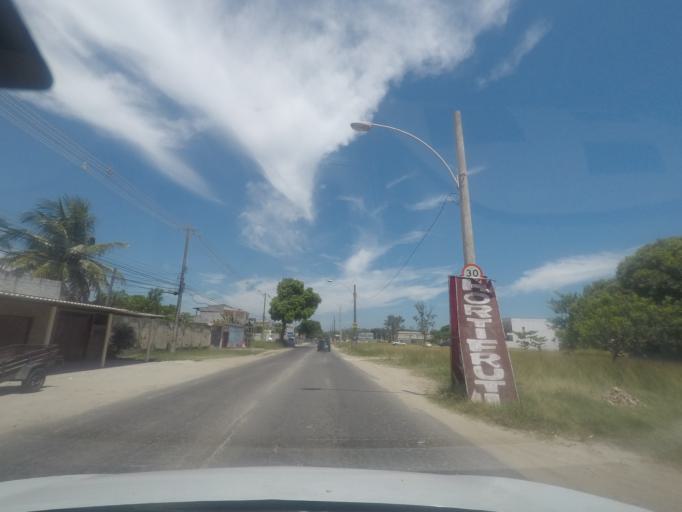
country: BR
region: Rio de Janeiro
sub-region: Itaguai
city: Itaguai
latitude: -22.9821
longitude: -43.6635
